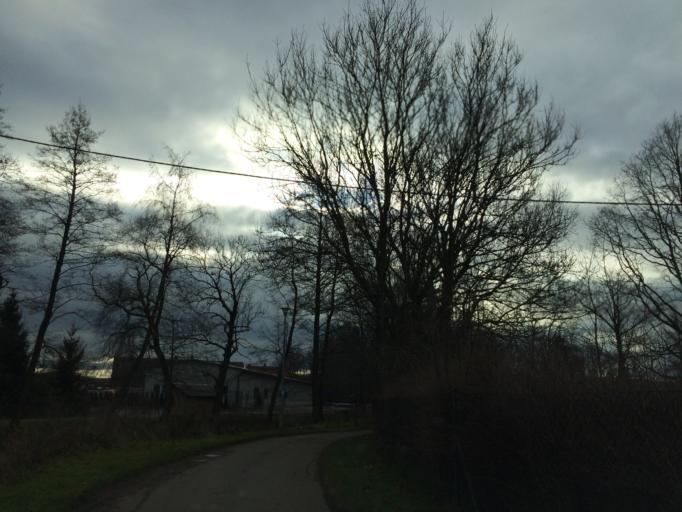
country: PL
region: Lower Silesian Voivodeship
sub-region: Powiat lwowecki
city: Lwowek Slaski
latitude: 51.0930
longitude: 15.5947
